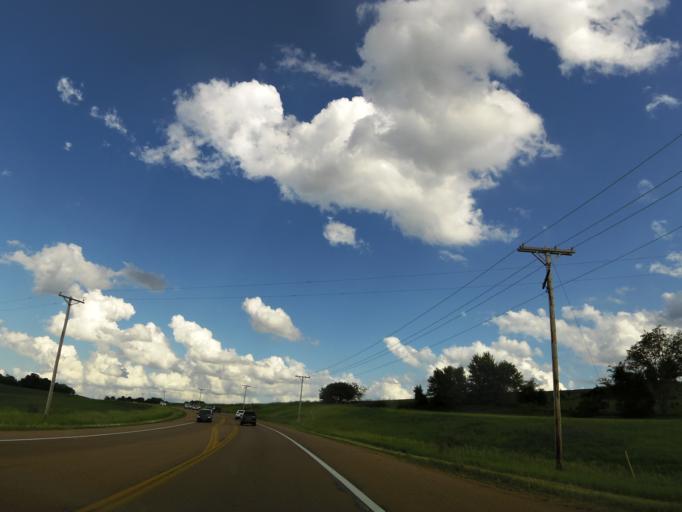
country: US
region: Minnesota
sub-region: Carver County
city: Waconia
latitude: 44.8301
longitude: -93.7591
